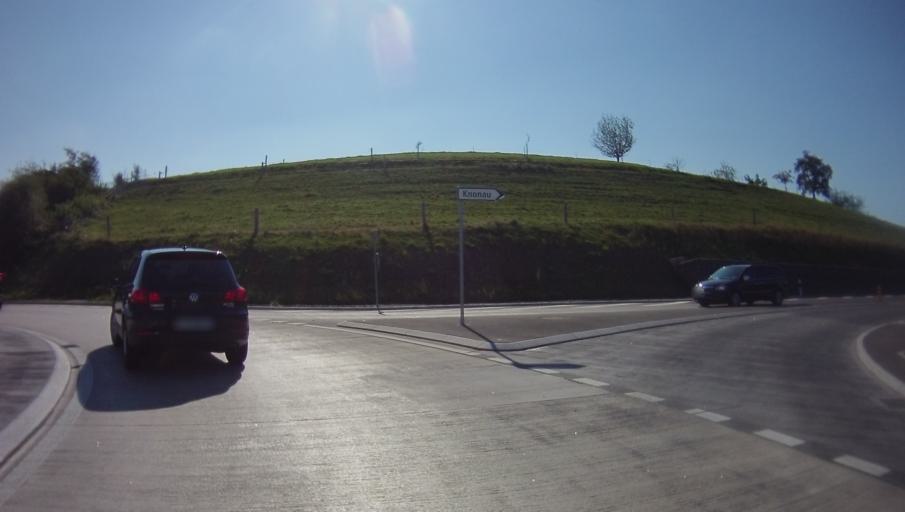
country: CH
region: Zug
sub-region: Zug
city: Steinhausen
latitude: 47.1960
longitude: 8.4751
